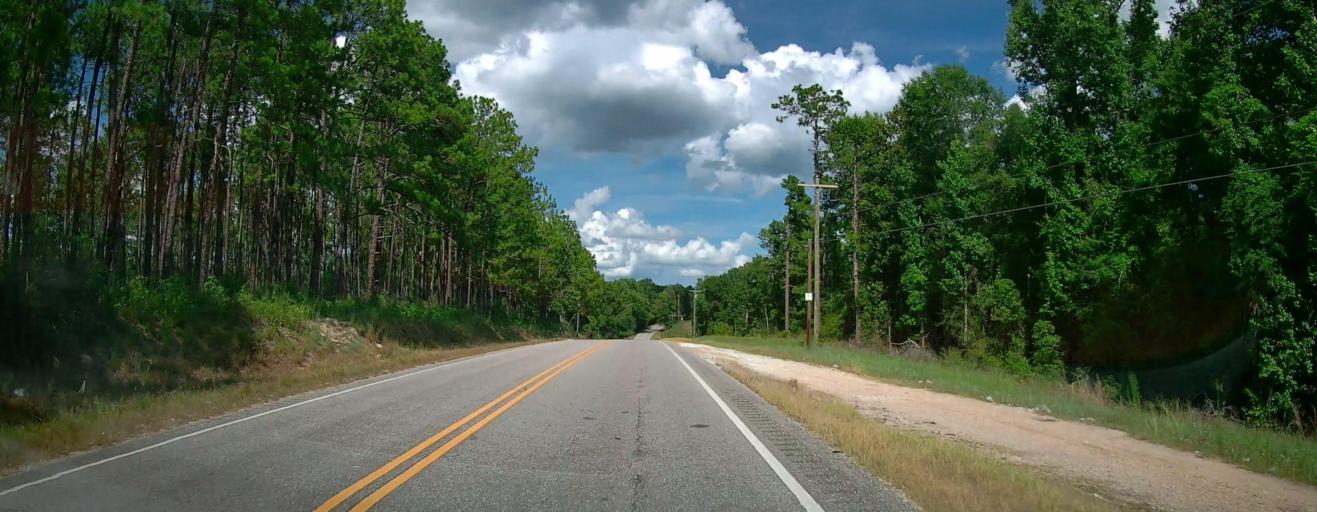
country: US
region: Alabama
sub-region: Macon County
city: Tuskegee
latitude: 32.4603
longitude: -85.6147
